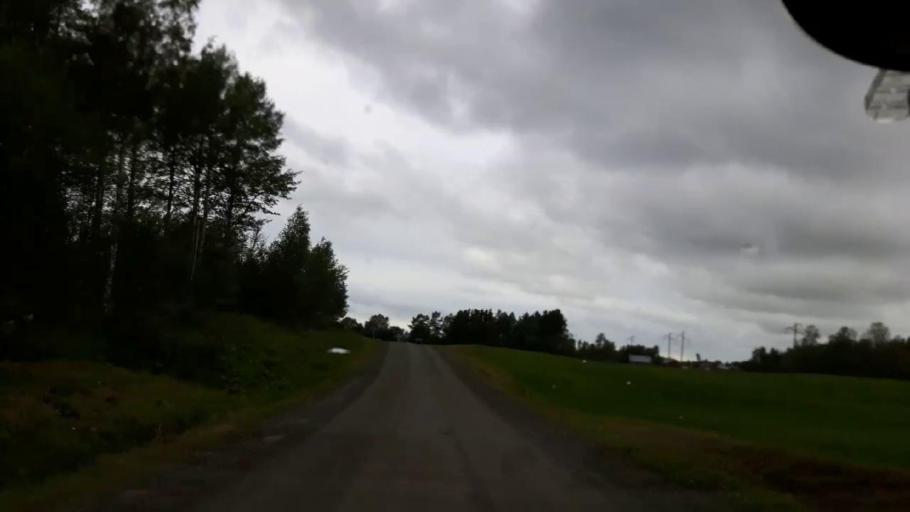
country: SE
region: Jaemtland
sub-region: OEstersunds Kommun
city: Ostersund
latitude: 63.0477
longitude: 14.5721
